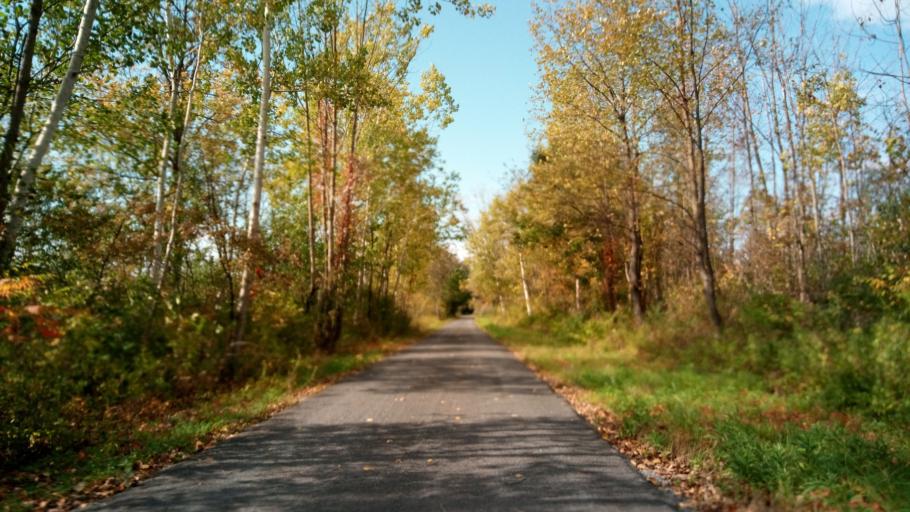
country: US
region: New York
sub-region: Wayne County
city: Clyde
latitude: 43.0696
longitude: -76.8563
